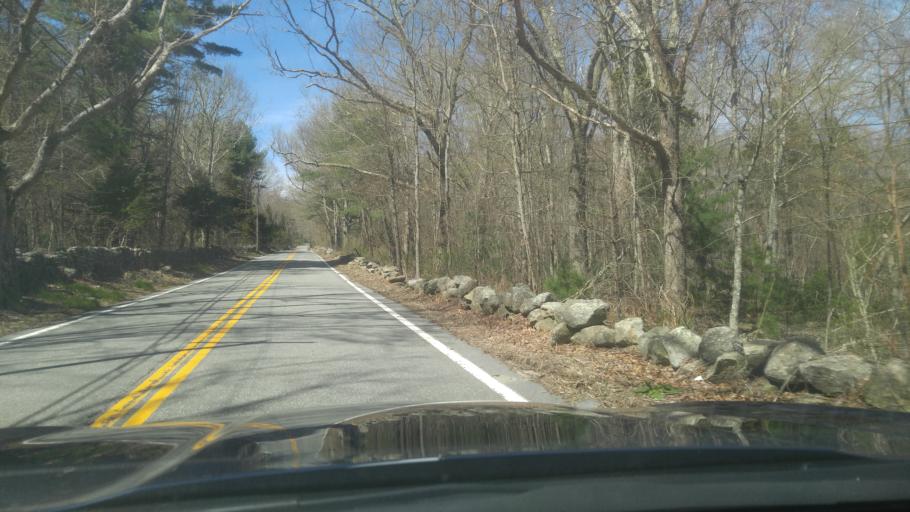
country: US
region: Rhode Island
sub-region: Washington County
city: Hope Valley
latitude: 41.5830
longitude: -71.7572
